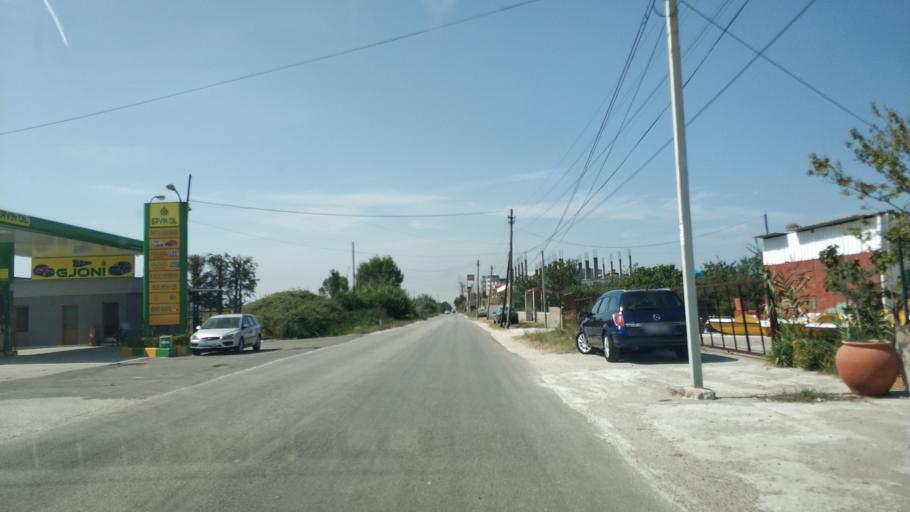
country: AL
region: Fier
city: Fier
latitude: 40.7326
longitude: 19.5340
